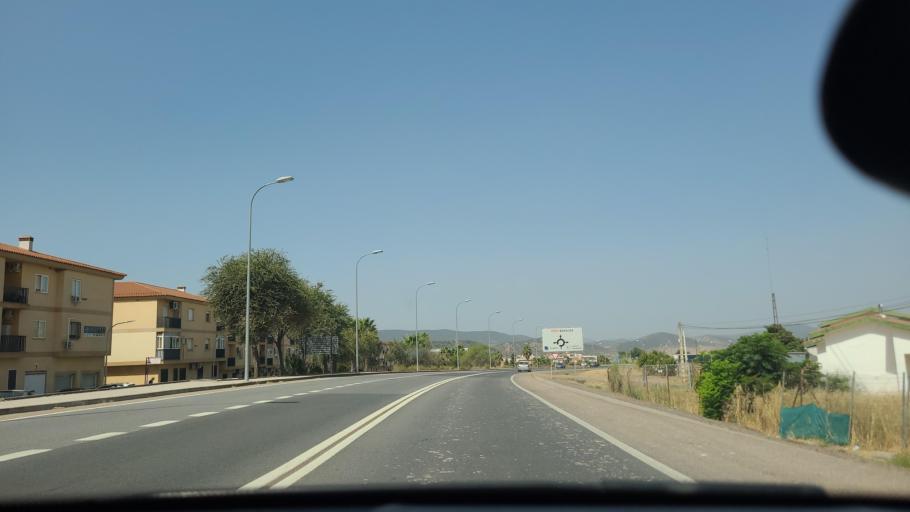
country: ES
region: Extremadura
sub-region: Provincia de Badajoz
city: Zafra
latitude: 38.4306
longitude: -6.4176
